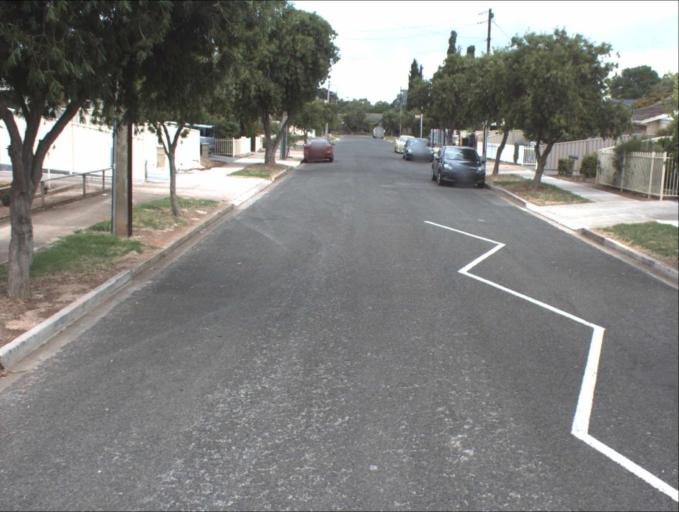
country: AU
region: South Australia
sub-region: Port Adelaide Enfield
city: Enfield
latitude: -34.8501
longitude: 138.6196
